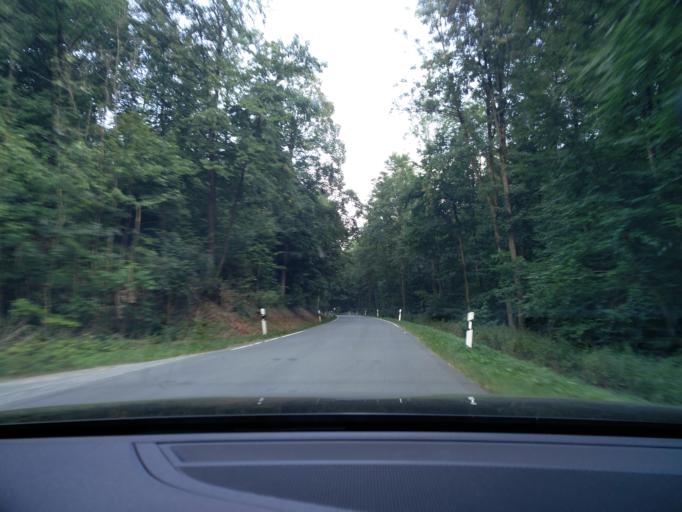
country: DE
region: North Rhine-Westphalia
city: Lichtenau
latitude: 51.6901
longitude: 8.9002
